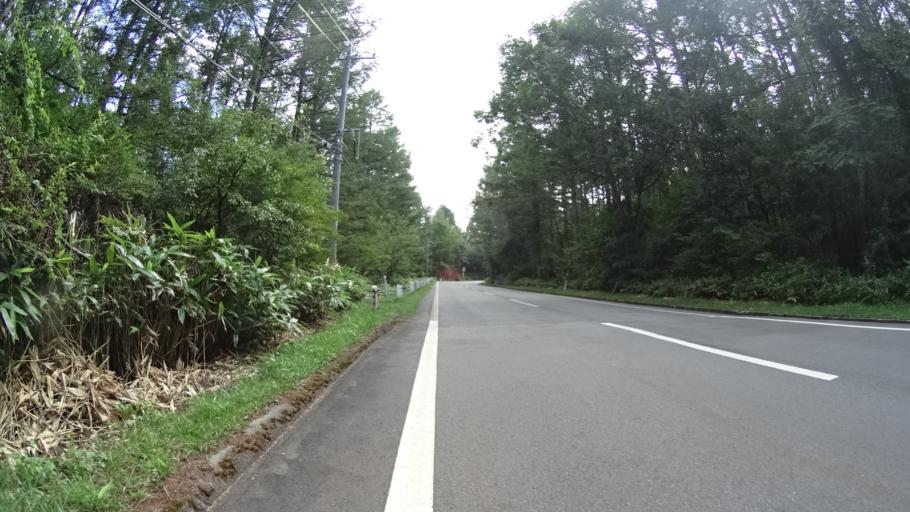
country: JP
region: Nagano
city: Saku
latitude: 36.0487
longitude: 138.4121
